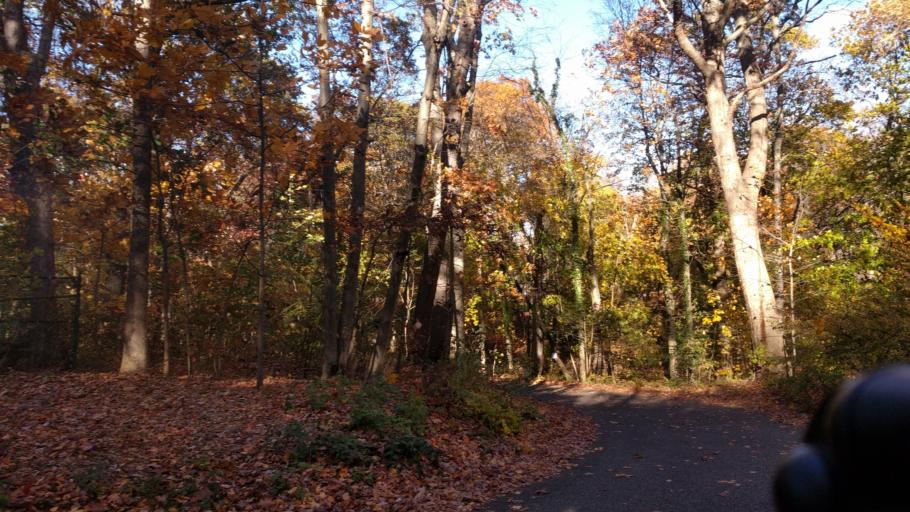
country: US
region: New York
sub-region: Nassau County
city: Bayville
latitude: 40.8948
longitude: -73.5550
